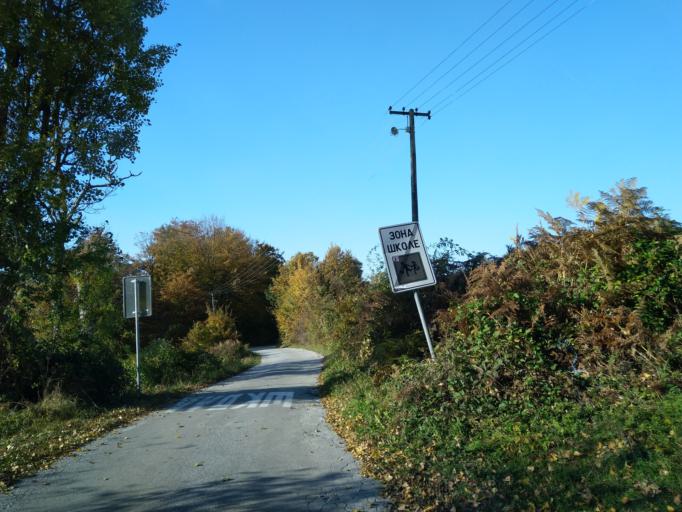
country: RS
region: Central Serbia
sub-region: Zlatiborski Okrug
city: Uzice
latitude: 43.8710
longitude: 19.7546
